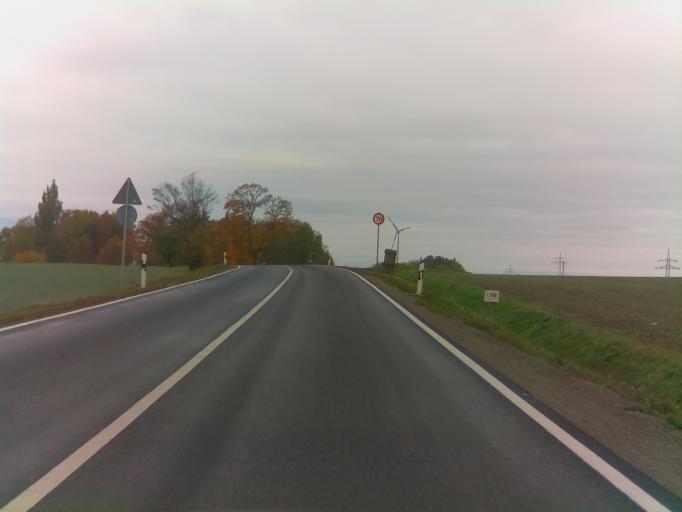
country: DE
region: Thuringia
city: Stadtilm
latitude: 50.7892
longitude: 11.0544
